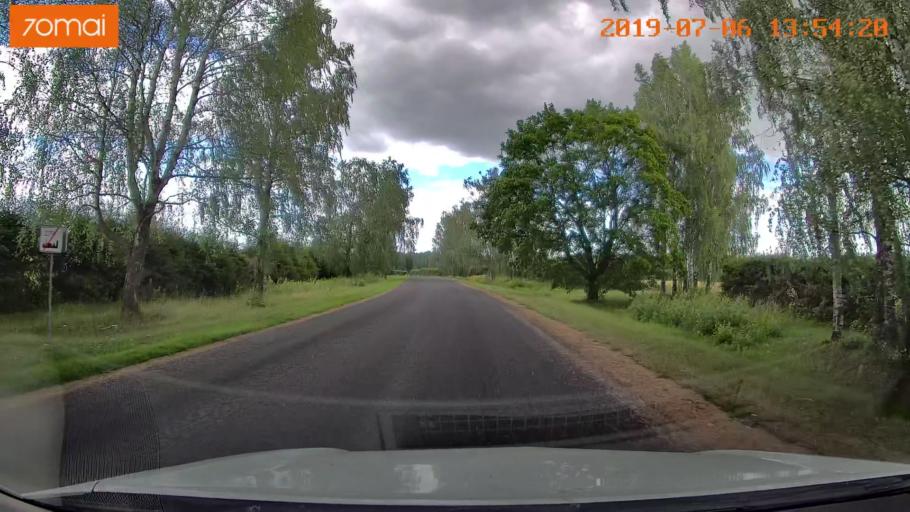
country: BY
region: Minsk
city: Ivyanyets
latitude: 53.7447
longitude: 26.8214
